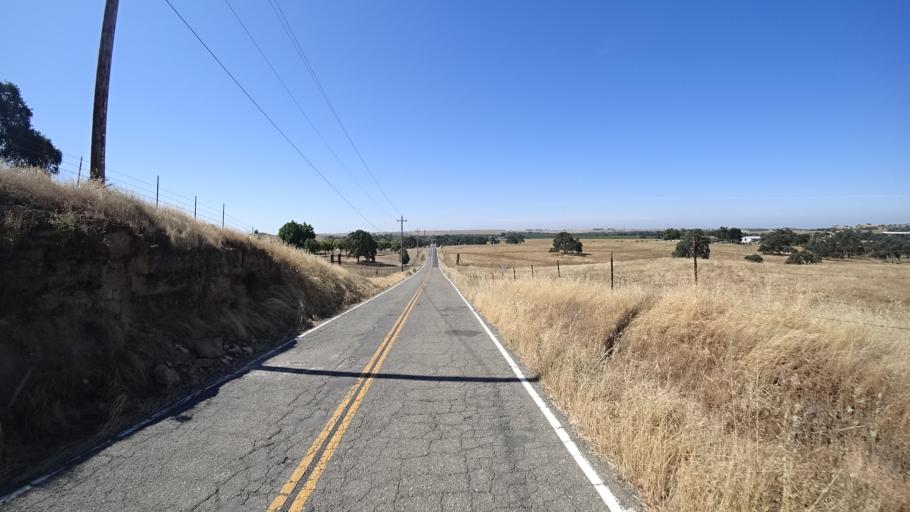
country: US
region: California
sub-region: Calaveras County
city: Rancho Calaveras
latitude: 38.0934
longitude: -120.9265
